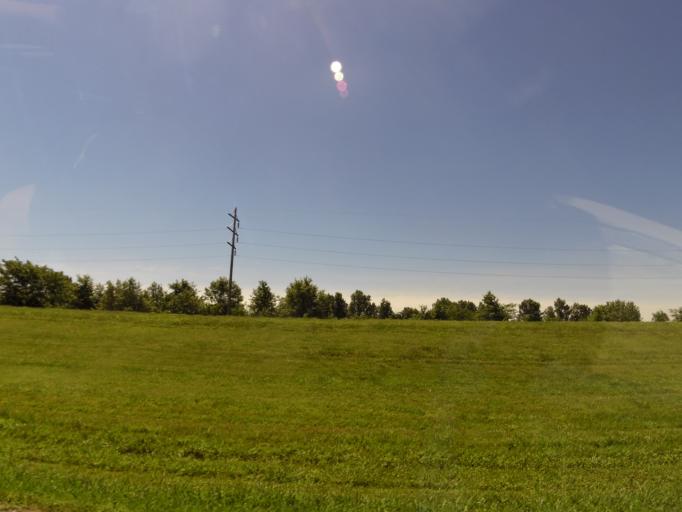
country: US
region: Missouri
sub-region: New Madrid County
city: New Madrid
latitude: 36.5780
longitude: -89.5619
